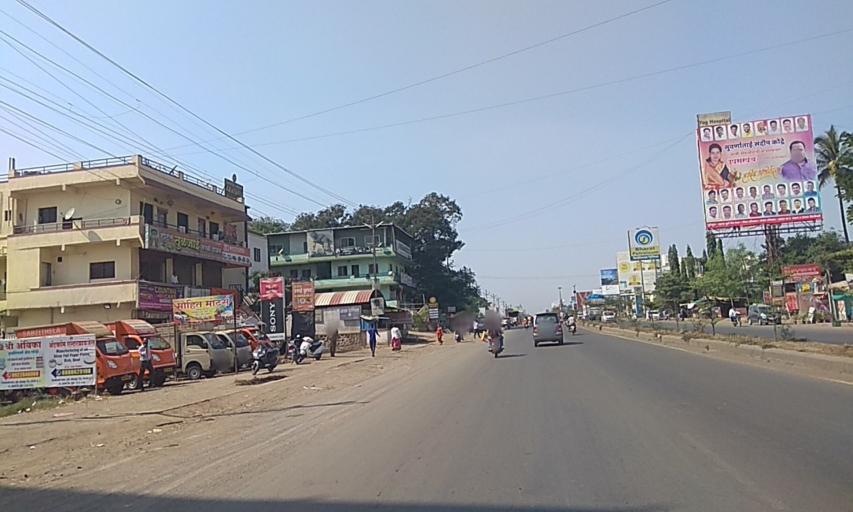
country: IN
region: Maharashtra
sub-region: Pune Division
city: Lohogaon
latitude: 18.4966
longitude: 73.9688
